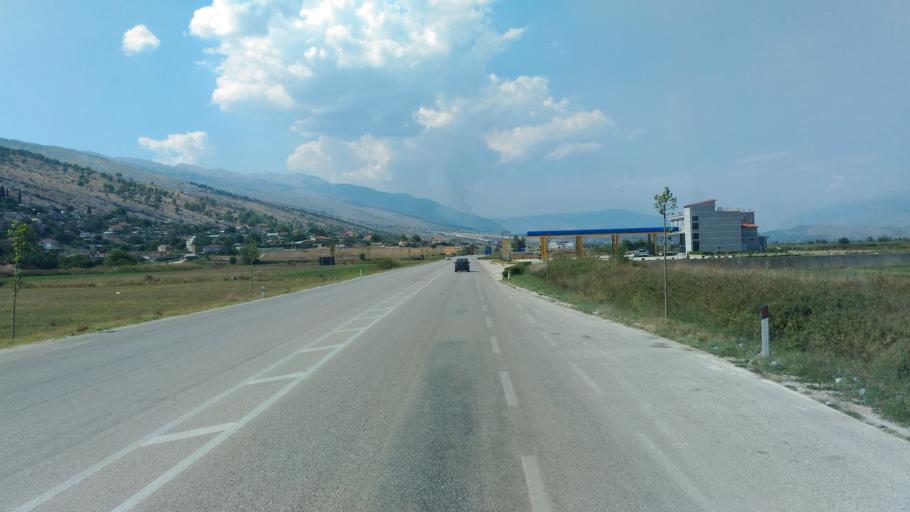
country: AL
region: Gjirokaster
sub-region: Rrethi i Gjirokastres
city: Dervician
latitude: 40.0139
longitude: 20.1996
